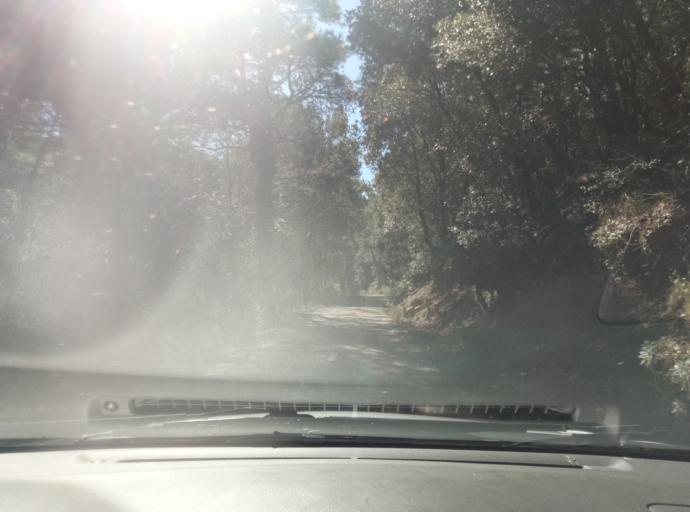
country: ES
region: Catalonia
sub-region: Provincia de Tarragona
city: Capafonts
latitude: 41.3405
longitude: 1.0567
